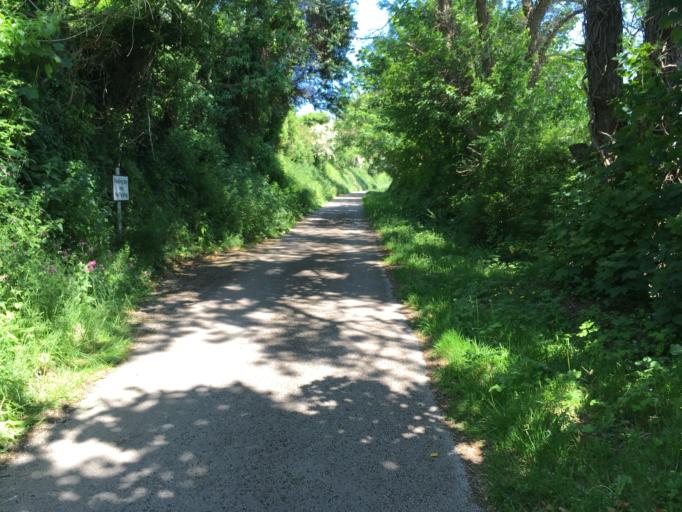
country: GB
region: England
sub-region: Devon
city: Dartmouth
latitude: 50.3436
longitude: -3.5581
